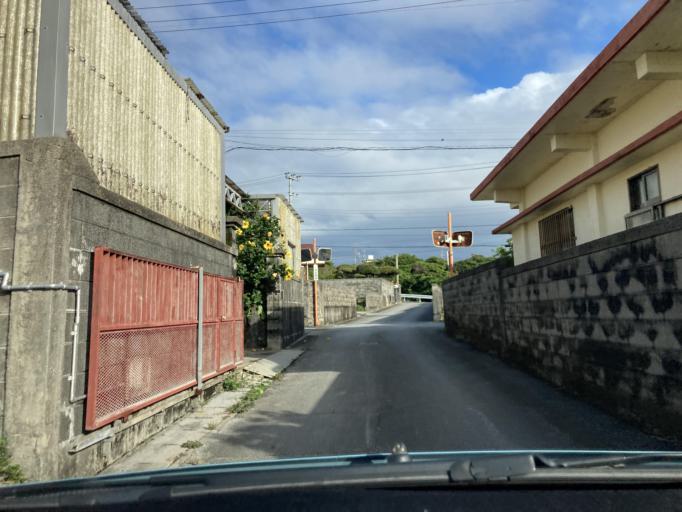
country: JP
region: Okinawa
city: Itoman
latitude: 26.1060
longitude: 127.6629
